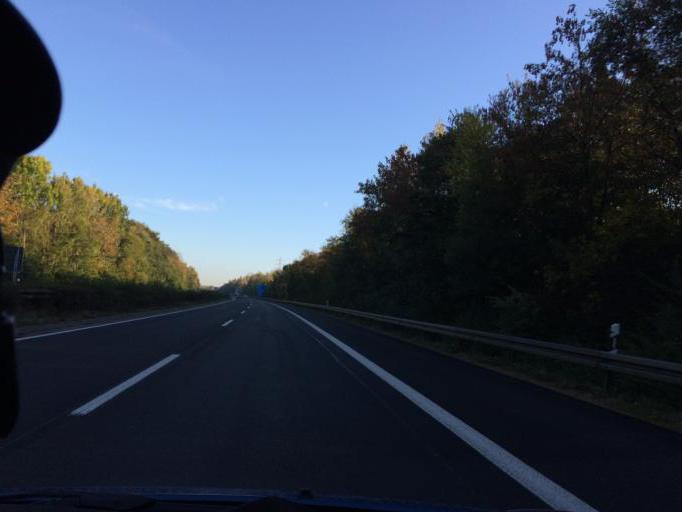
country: DE
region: North Rhine-Westphalia
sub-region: Regierungsbezirk Koln
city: Erftstadt
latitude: 50.8403
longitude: 6.7990
